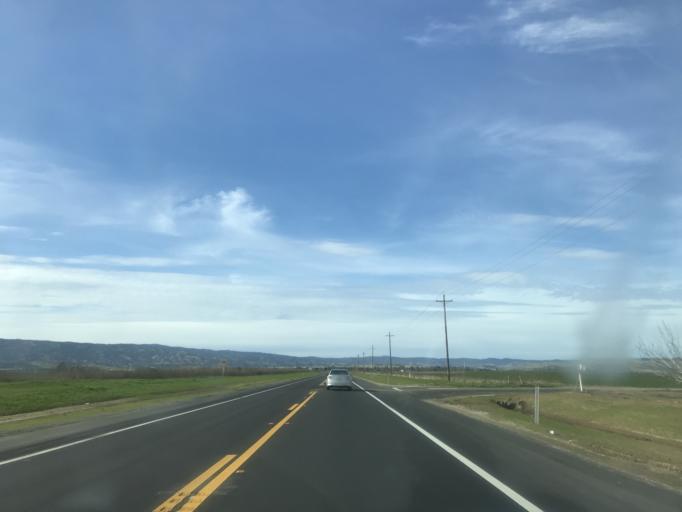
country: US
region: California
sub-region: Yolo County
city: Cottonwood
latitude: 38.6843
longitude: -121.9842
